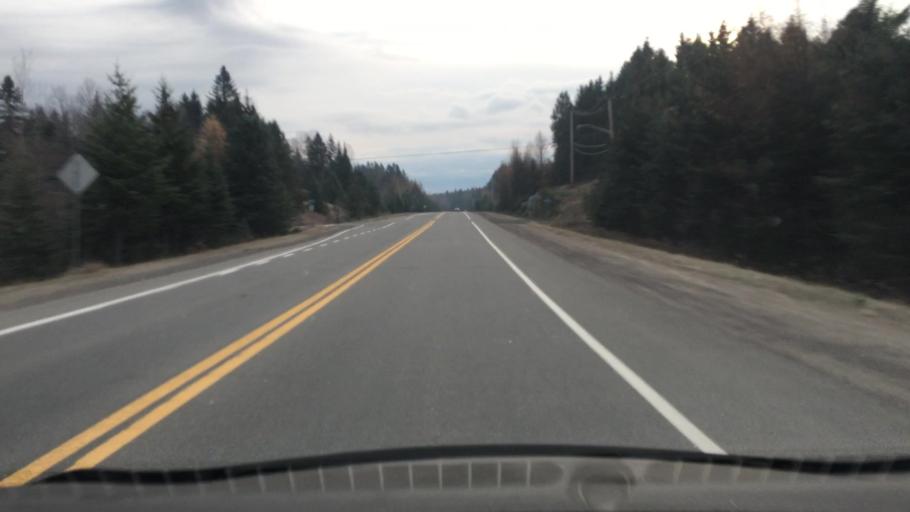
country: CA
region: Quebec
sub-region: Laurentides
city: Saint-Sauveur
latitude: 45.9030
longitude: -74.2335
